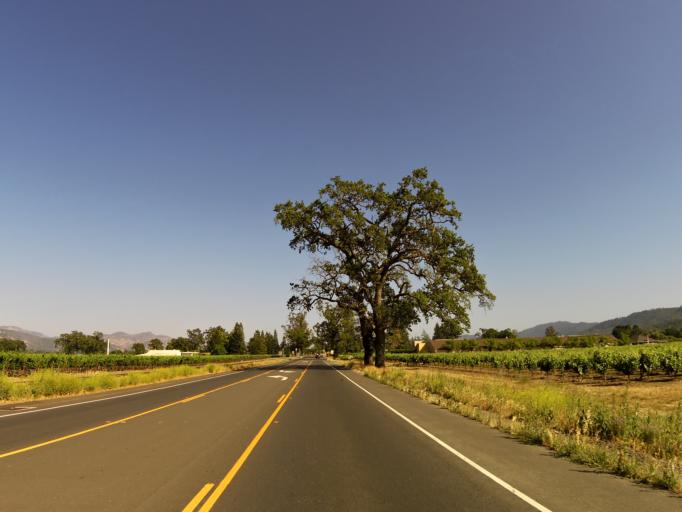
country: US
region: California
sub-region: Napa County
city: Saint Helena
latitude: 38.4797
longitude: -122.4392
